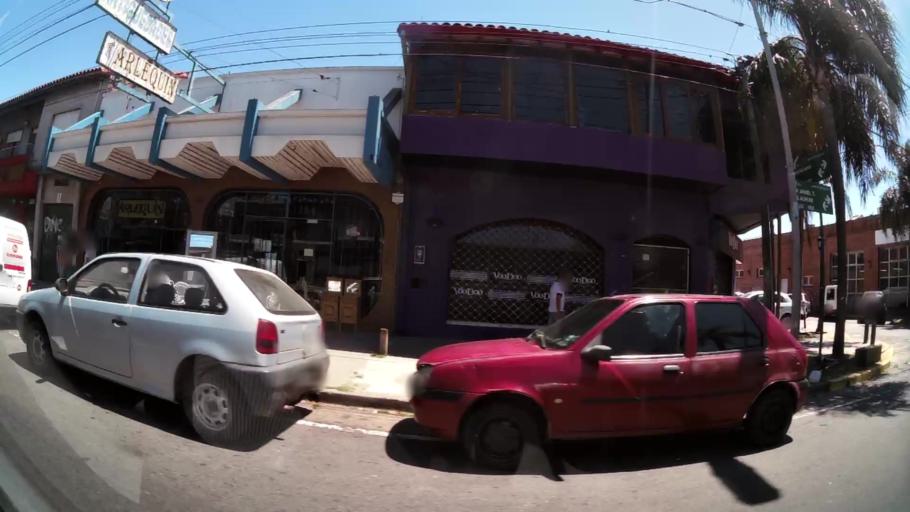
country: AR
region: Buenos Aires
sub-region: Partido de Tigre
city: Tigre
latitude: -34.4949
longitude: -58.6330
